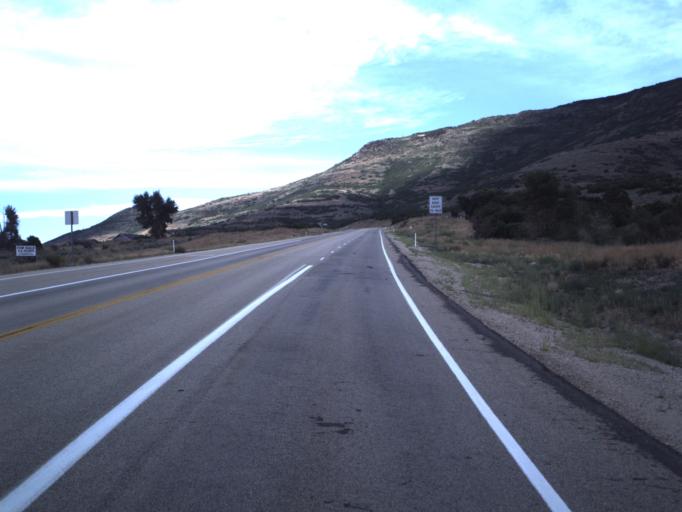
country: US
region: Utah
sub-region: Wasatch County
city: Heber
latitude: 40.5629
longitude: -111.4238
